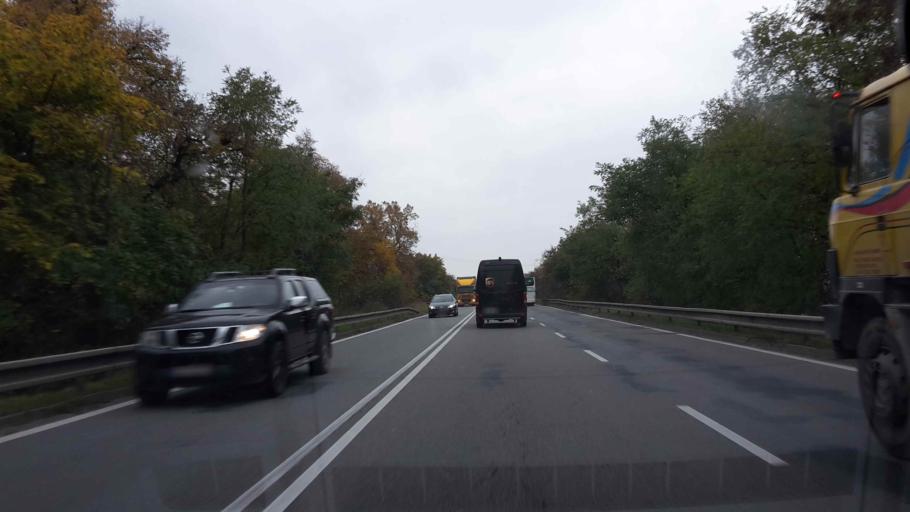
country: CZ
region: South Moravian
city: Slavkov u Brna
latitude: 49.1594
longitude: 16.8571
